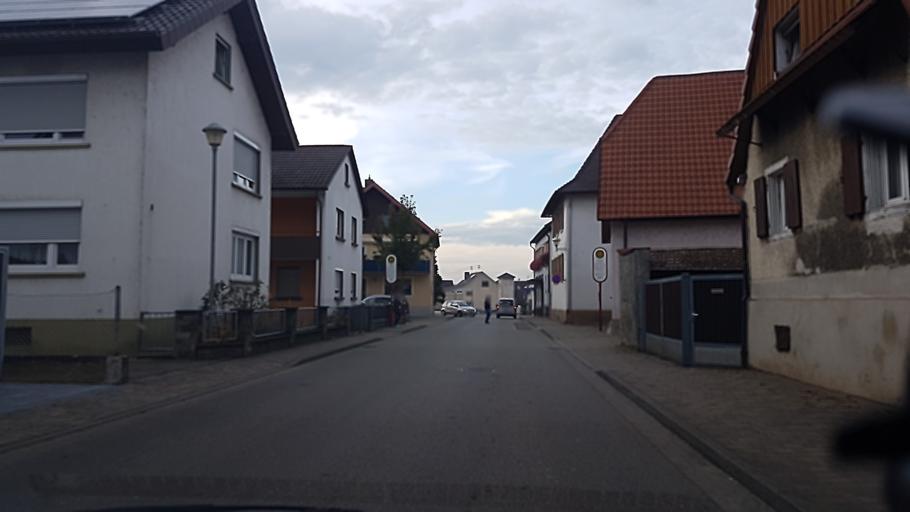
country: DE
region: Baden-Wuerttemberg
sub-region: Freiburg Region
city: Wyhl
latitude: 48.1654
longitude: 7.6500
